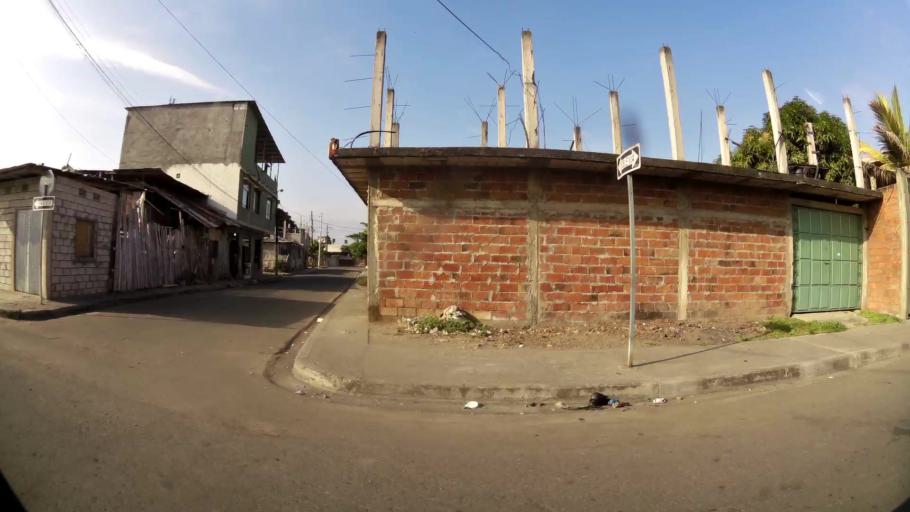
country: EC
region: Guayas
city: Eloy Alfaro
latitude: -2.1823
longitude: -79.8498
